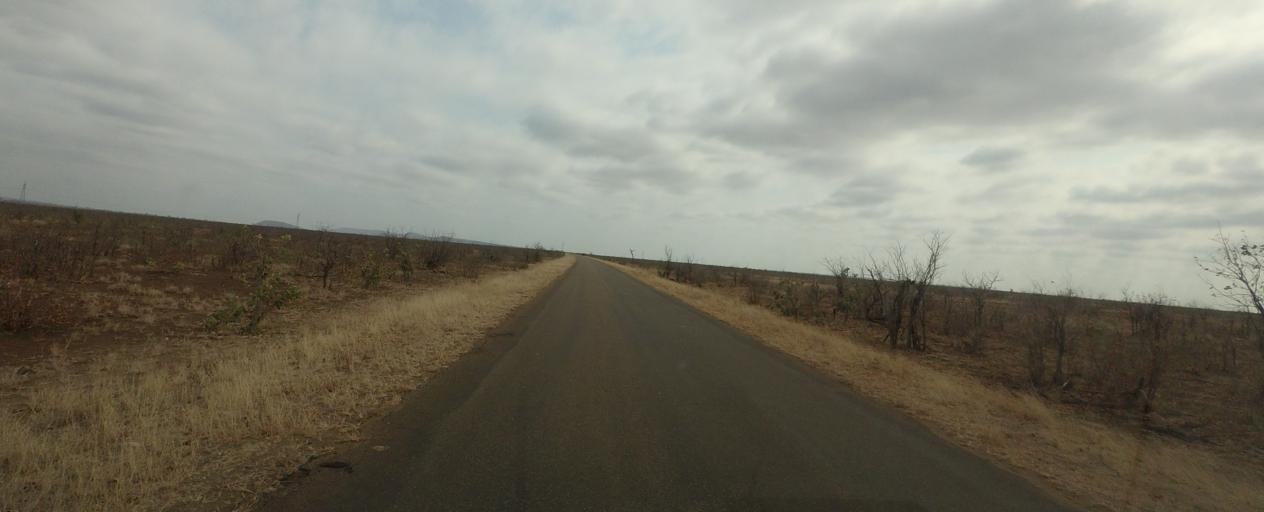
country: ZA
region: Limpopo
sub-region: Vhembe District Municipality
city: Mutale
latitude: -22.6751
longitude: 31.1676
